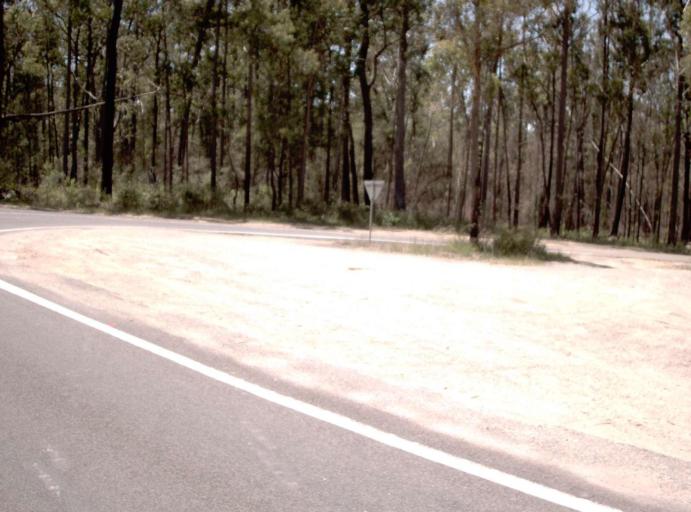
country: AU
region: Victoria
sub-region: East Gippsland
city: Lakes Entrance
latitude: -37.7543
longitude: 148.0670
